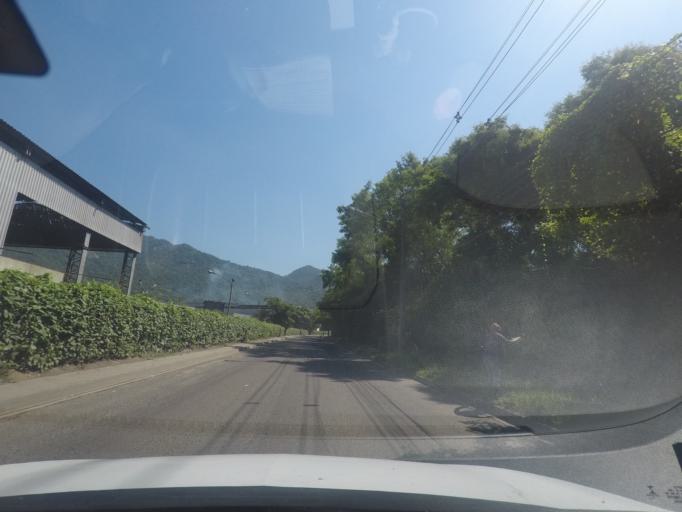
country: BR
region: Rio de Janeiro
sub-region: Nilopolis
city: Nilopolis
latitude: -22.9870
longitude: -43.4533
